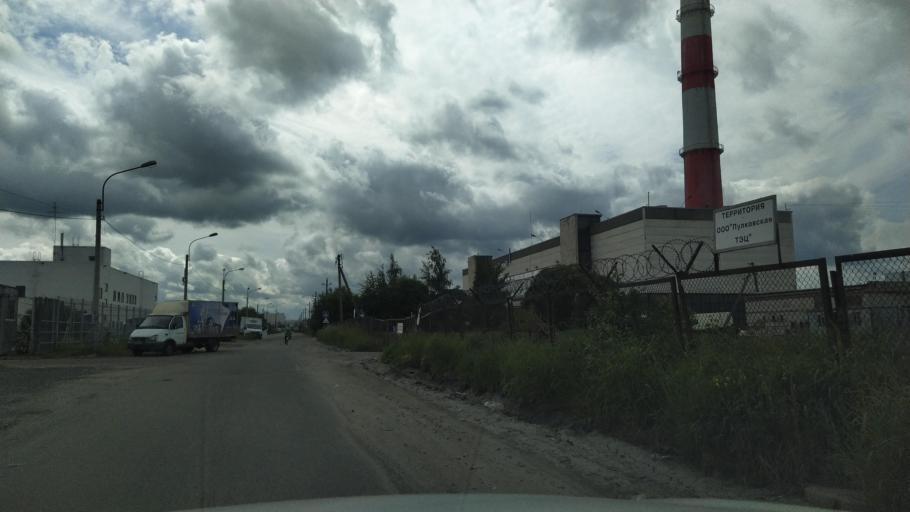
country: RU
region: St.-Petersburg
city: Kupchino
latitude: 59.8291
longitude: 30.3146
